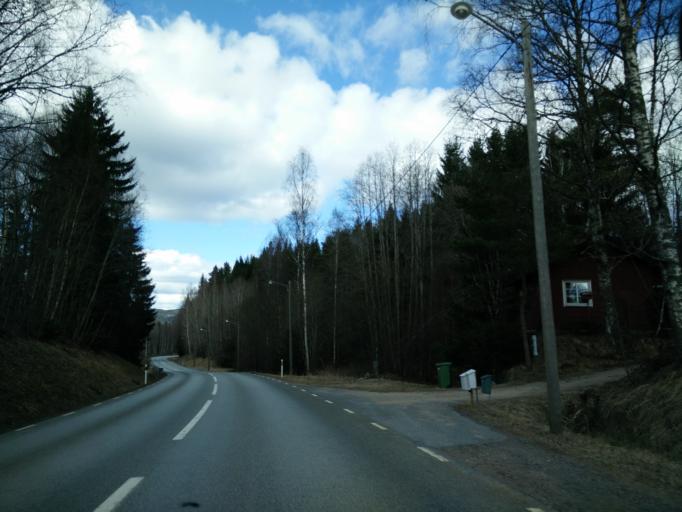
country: SE
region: Vaermland
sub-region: Munkfors Kommun
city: Munkfors
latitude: 59.8897
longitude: 13.5643
